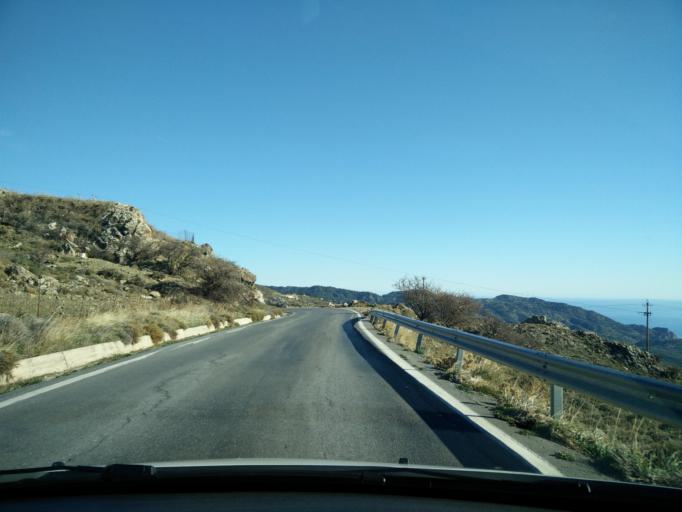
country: GR
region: Crete
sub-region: Nomos Irakleiou
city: Kastelli
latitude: 35.0441
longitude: 25.4260
